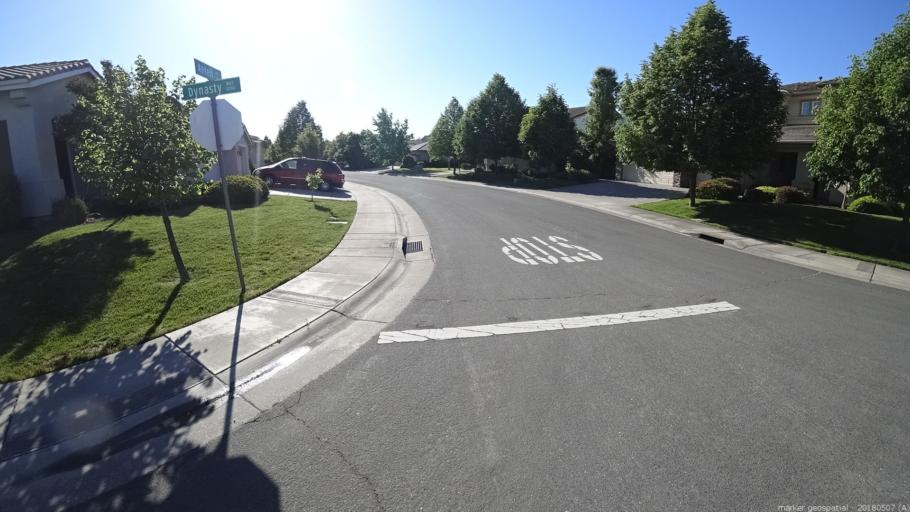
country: US
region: California
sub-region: Sacramento County
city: Rio Linda
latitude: 38.6685
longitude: -121.4969
